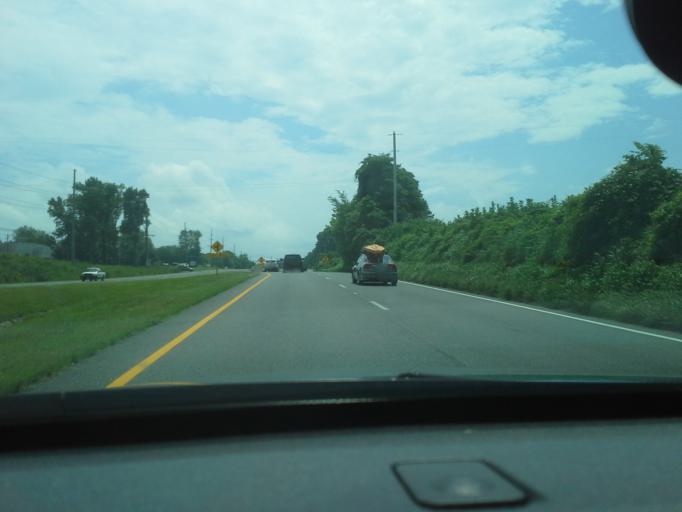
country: US
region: Maryland
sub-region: Calvert County
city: Dunkirk Town Center
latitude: 38.6938
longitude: -76.6413
